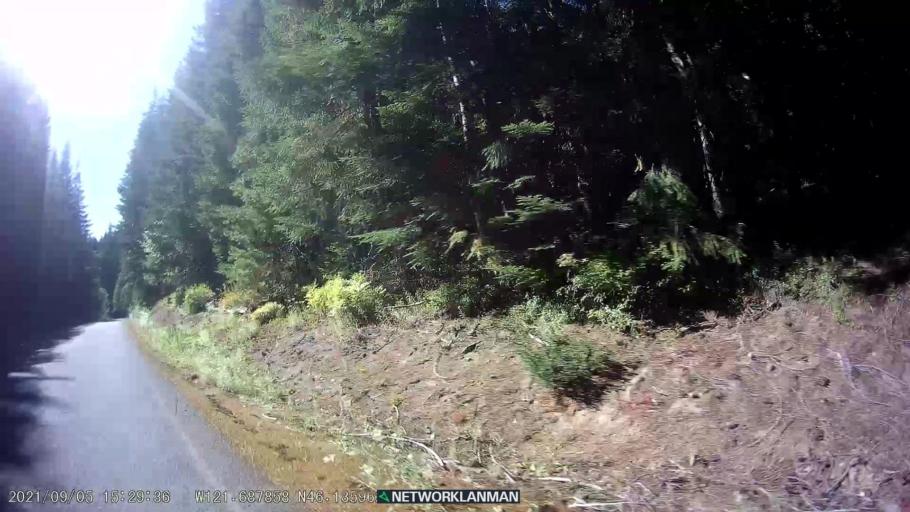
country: US
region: Washington
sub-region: Skamania County
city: Carson
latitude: 46.1358
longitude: -121.6881
